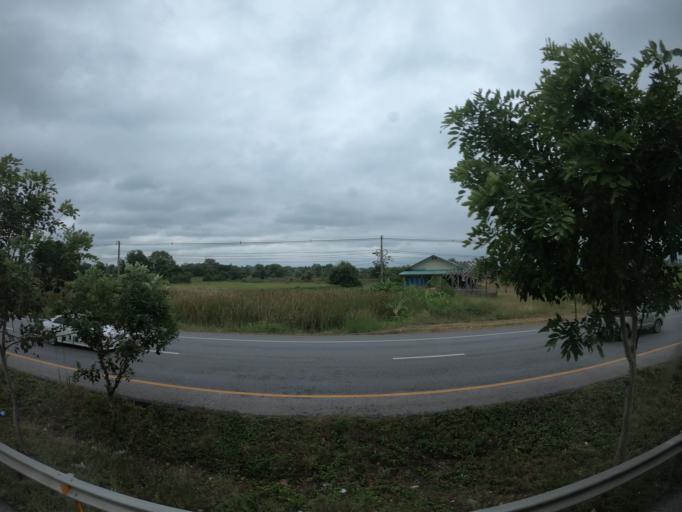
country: TH
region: Khon Kaen
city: Phon
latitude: 15.7851
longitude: 102.6069
